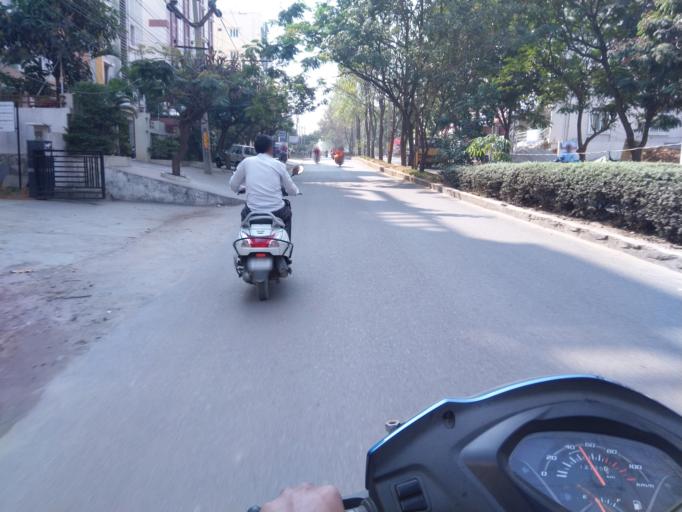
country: IN
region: Telangana
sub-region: Rangareddi
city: Kukatpalli
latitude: 17.4801
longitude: 78.3943
